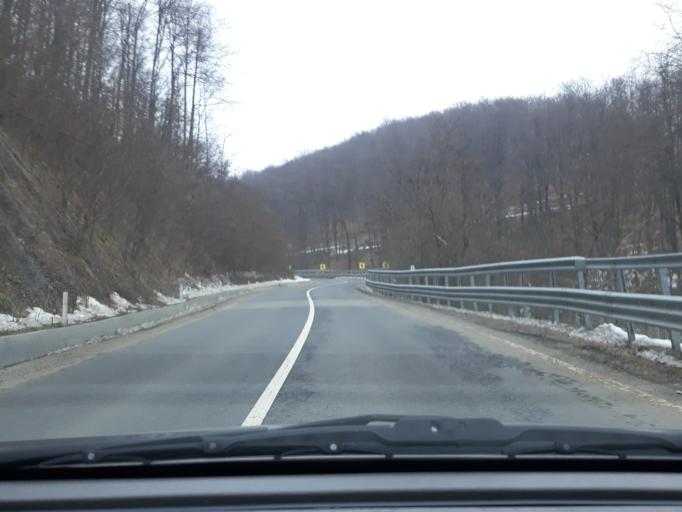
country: RO
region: Bihor
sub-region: Oras Alesd
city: Padurea Neagra
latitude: 47.1281
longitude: 22.4212
